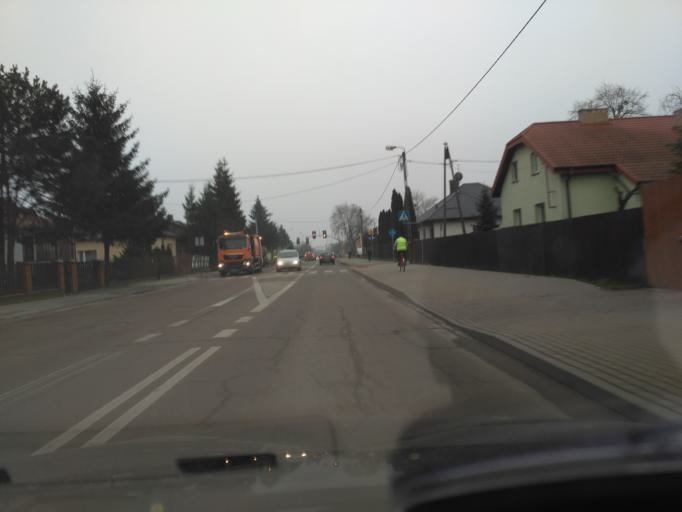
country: PL
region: Lublin Voivodeship
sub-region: Chelm
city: Chelm
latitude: 51.1463
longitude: 23.4564
